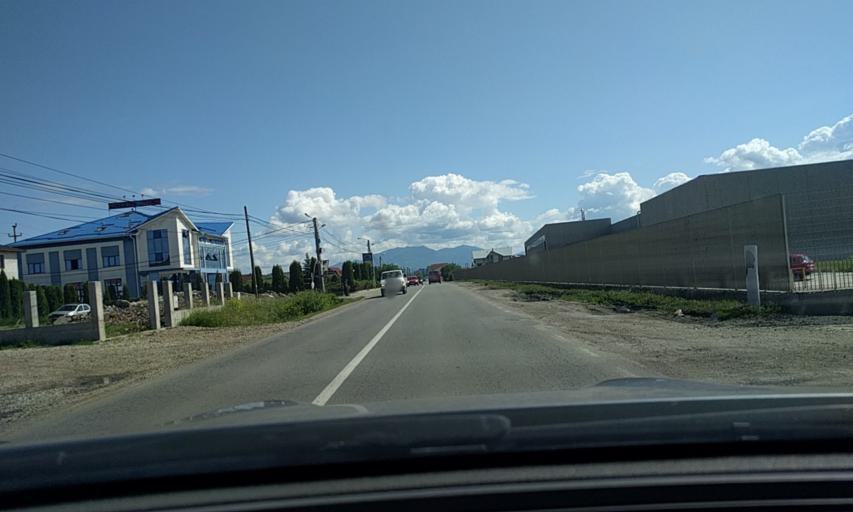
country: RO
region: Bistrita-Nasaud
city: Bistrita
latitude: 47.1511
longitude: 24.5024
